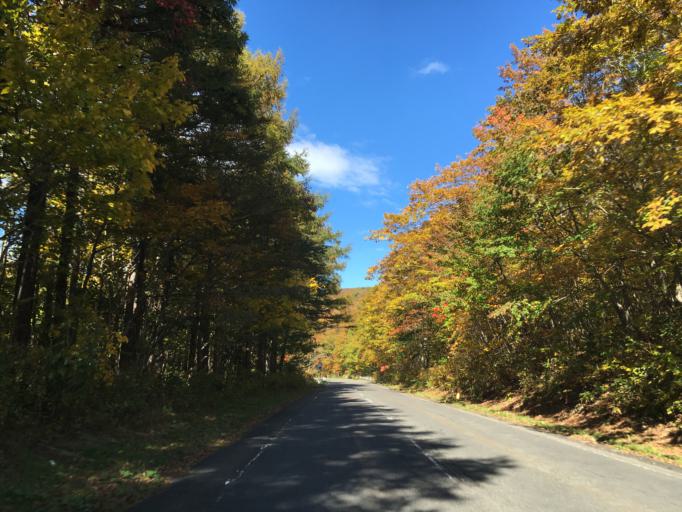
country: JP
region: Fukushima
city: Inawashiro
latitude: 37.5910
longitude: 140.2459
